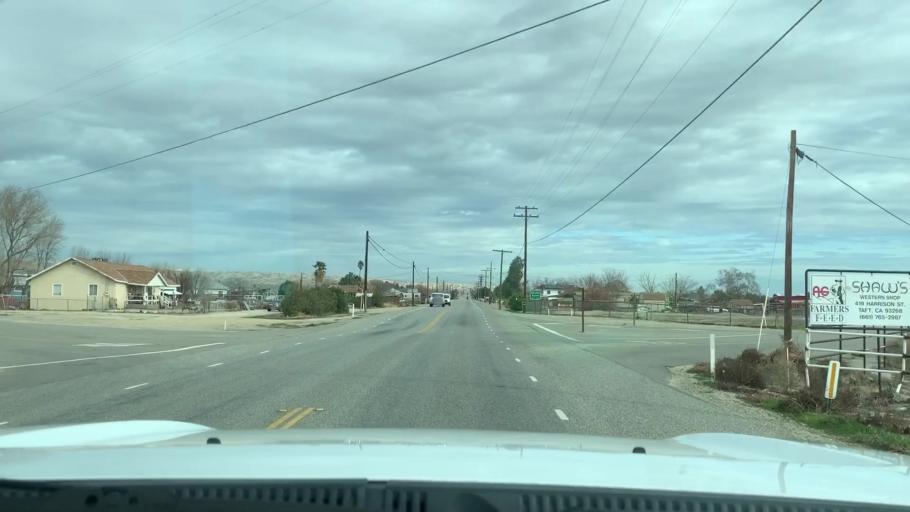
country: US
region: California
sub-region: Kern County
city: Ford City
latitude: 35.2171
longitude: -119.3940
